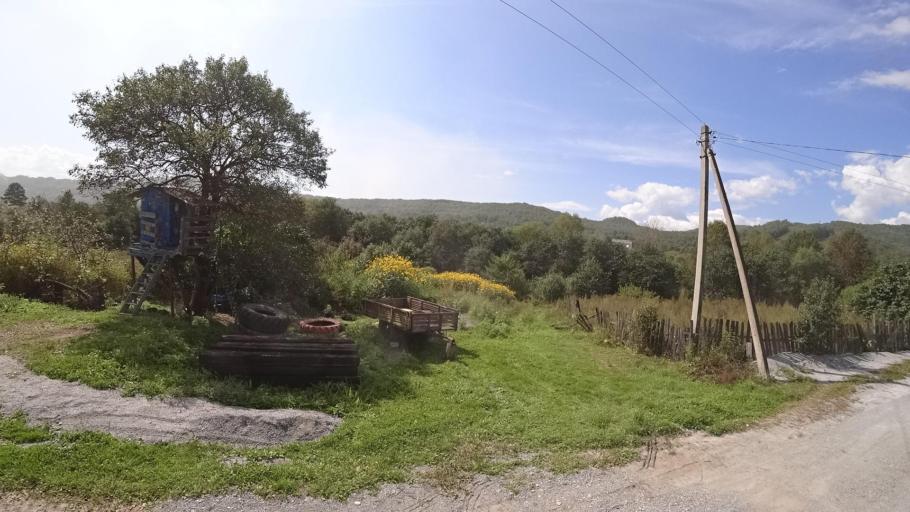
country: RU
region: Jewish Autonomous Oblast
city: Londoko
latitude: 49.0286
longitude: 131.9297
